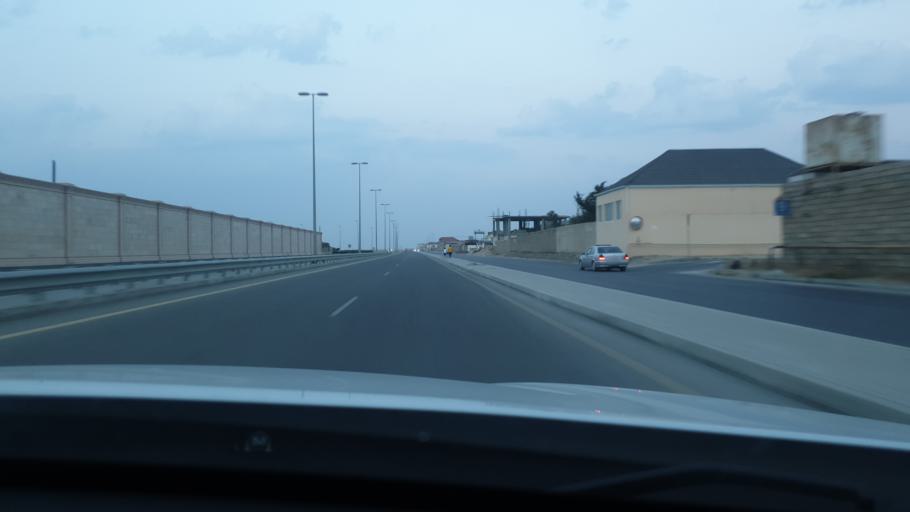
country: AZ
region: Baki
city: Bilajer
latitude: 40.5850
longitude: 50.0267
